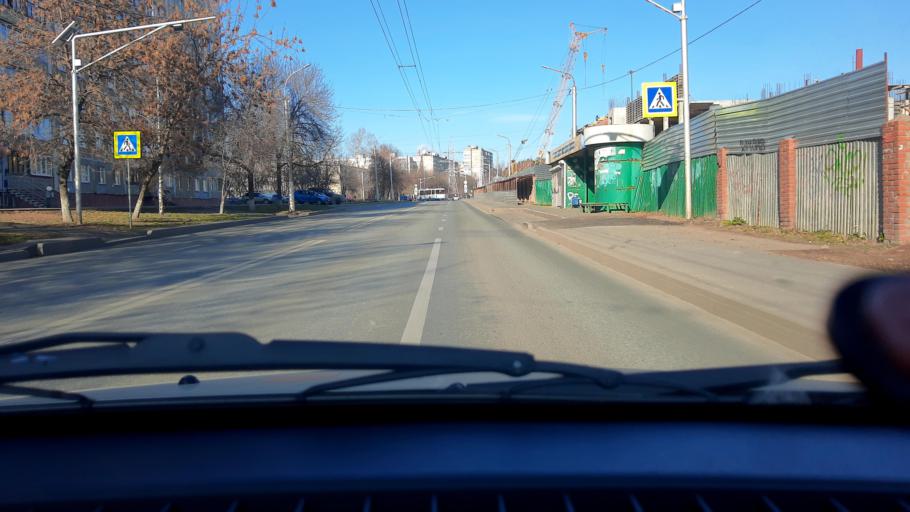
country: RU
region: Bashkortostan
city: Ufa
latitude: 54.7003
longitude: 56.0068
